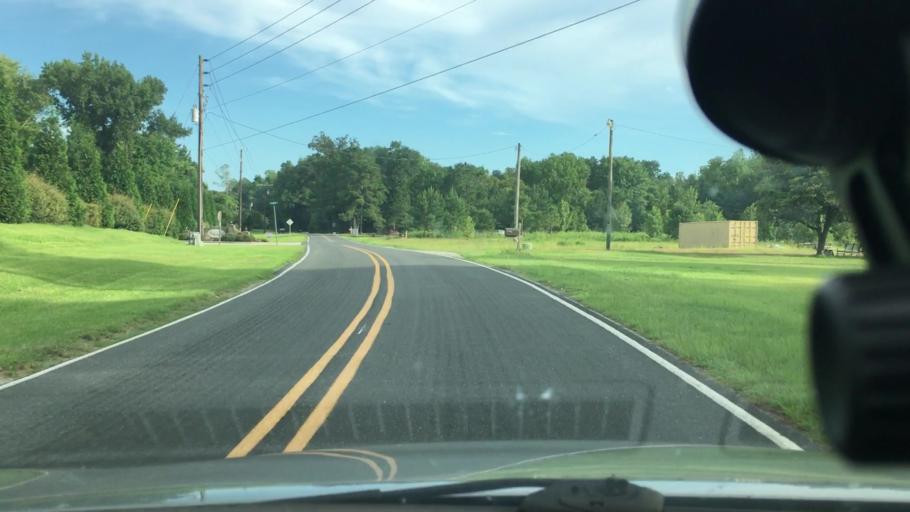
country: US
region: North Carolina
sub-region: Craven County
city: New Bern
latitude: 35.1845
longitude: -77.0583
